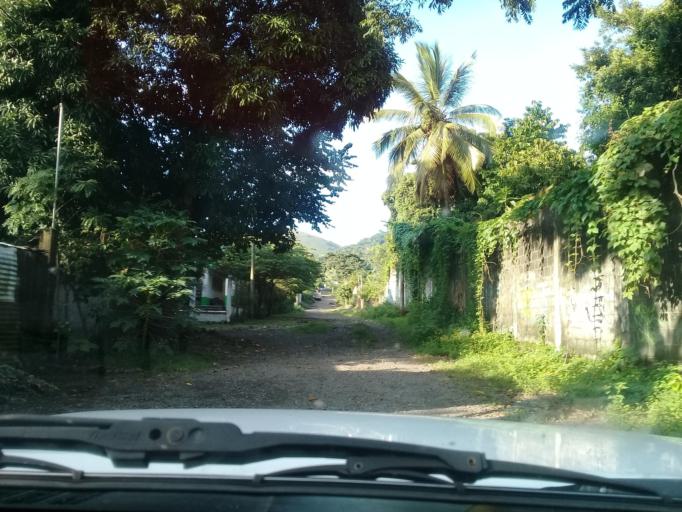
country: MX
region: Veracruz
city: Catemaco
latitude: 18.4229
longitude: -95.1025
